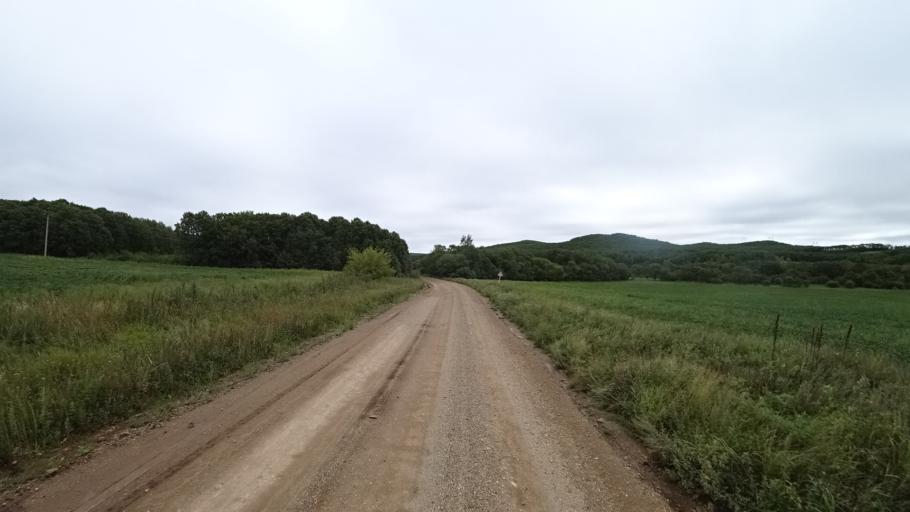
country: RU
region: Primorskiy
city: Ivanovka
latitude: 44.0577
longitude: 132.4779
